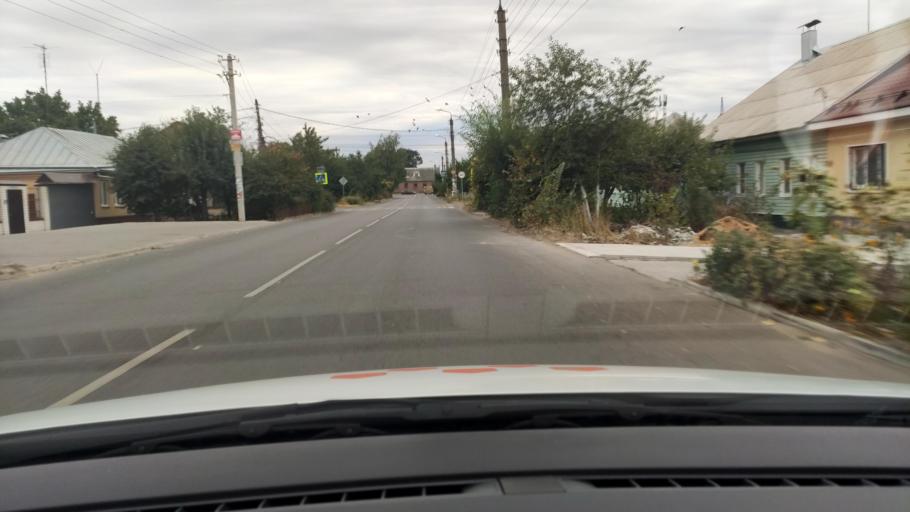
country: RU
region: Voronezj
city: Voronezh
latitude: 51.6397
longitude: 39.1682
